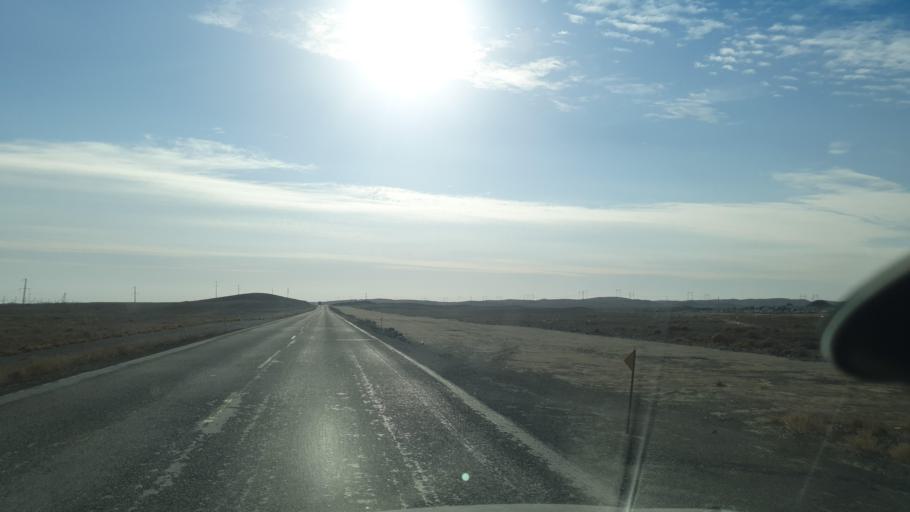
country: KZ
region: Zhambyl
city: Mynaral
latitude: 45.7262
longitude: 73.4045
